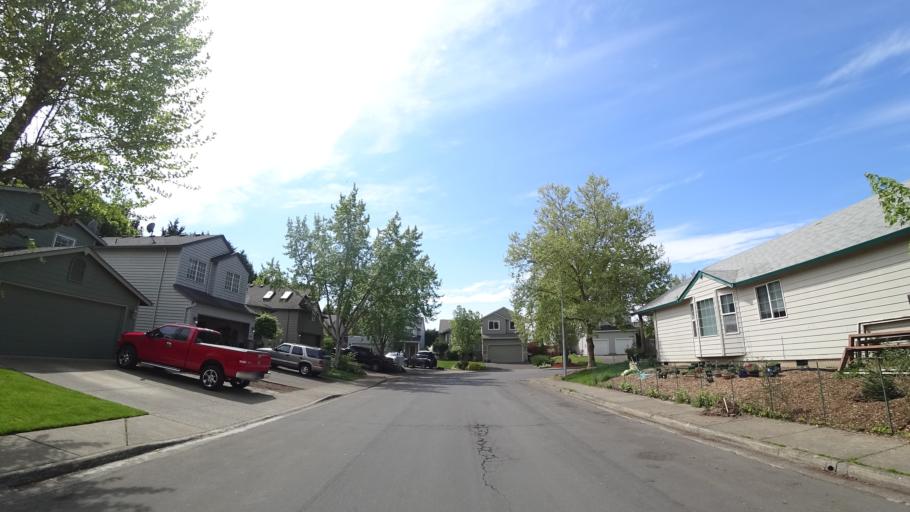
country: US
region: Oregon
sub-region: Washington County
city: Aloha
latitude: 45.4877
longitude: -122.8901
